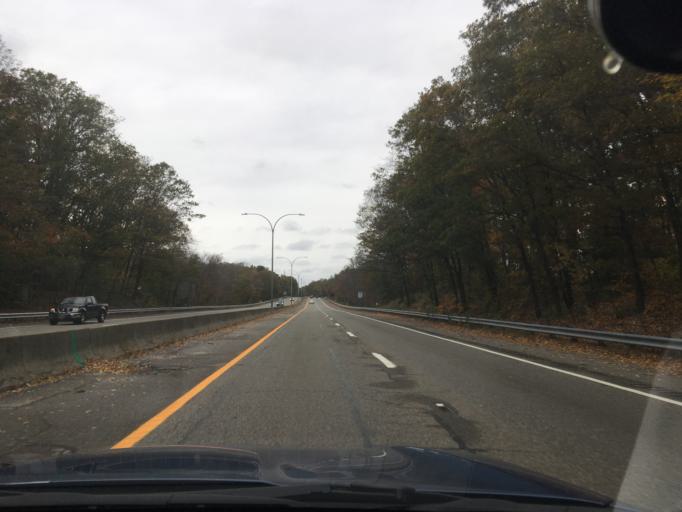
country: US
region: Massachusetts
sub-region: Bristol County
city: Seekonk
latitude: 41.7979
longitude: -71.3514
